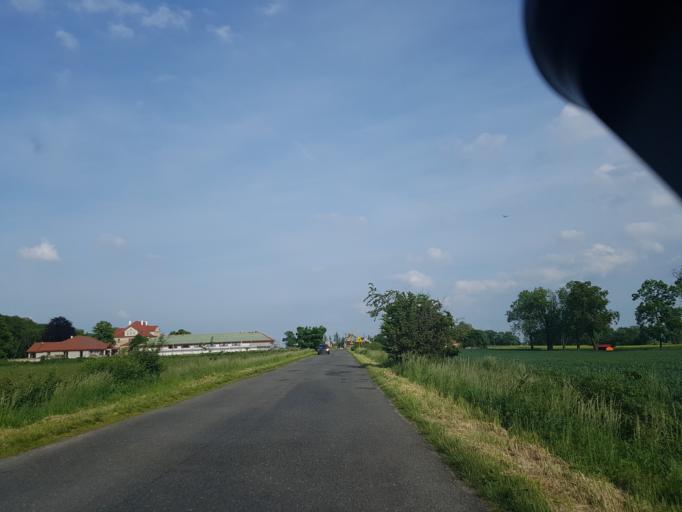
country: PL
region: Lower Silesian Voivodeship
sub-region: Powiat wroclawski
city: Zorawina
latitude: 50.9090
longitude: 17.0839
